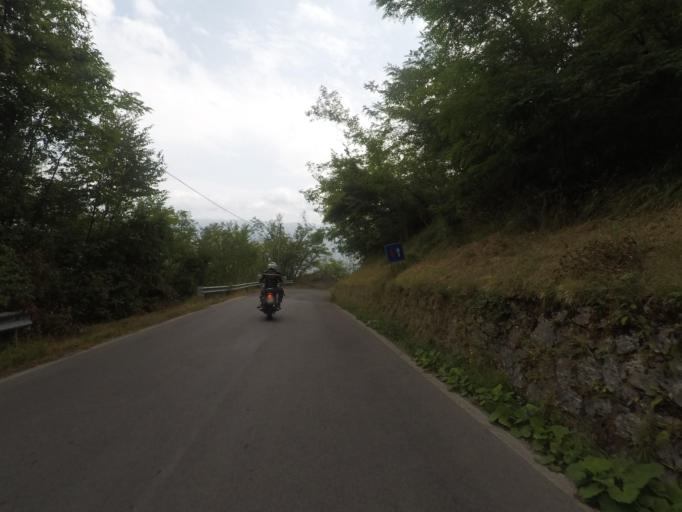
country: IT
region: Tuscany
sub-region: Provincia di Lucca
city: Castelnuovo di Garfagnana
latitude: 44.1111
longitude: 10.3675
